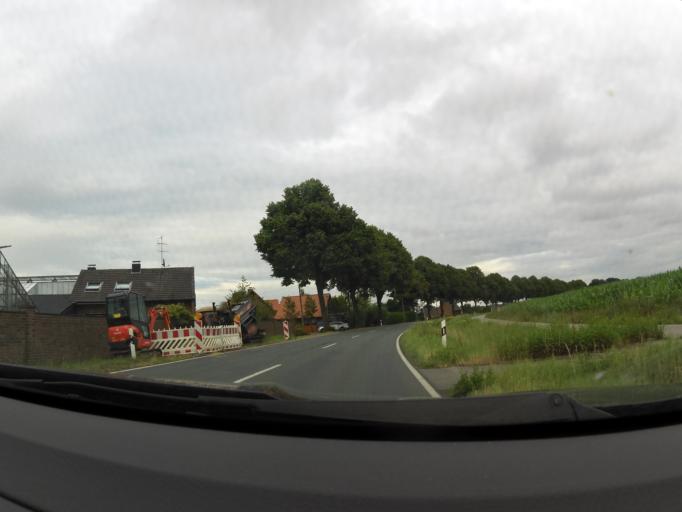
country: DE
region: North Rhine-Westphalia
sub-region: Regierungsbezirk Dusseldorf
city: Kevelaer
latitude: 51.5414
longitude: 6.2354
